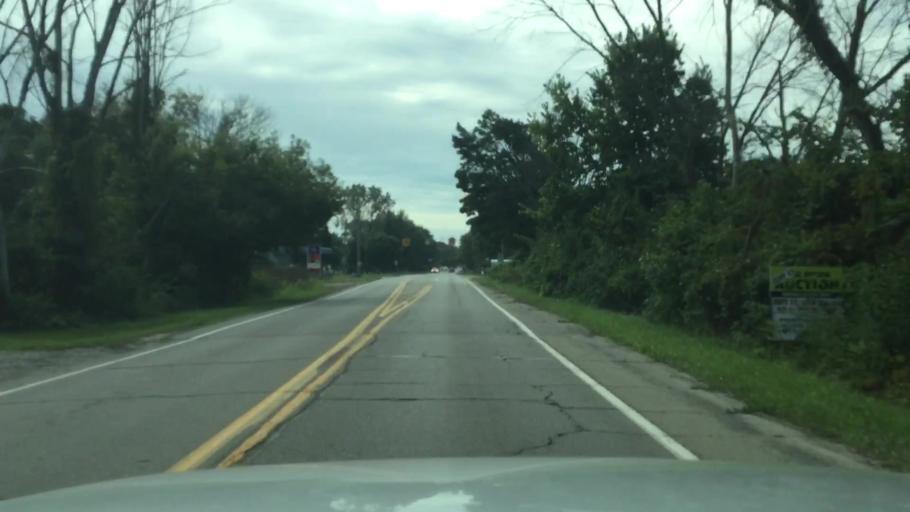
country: US
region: Michigan
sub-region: Wayne County
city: Belleville
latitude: 42.1768
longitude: -83.4829
